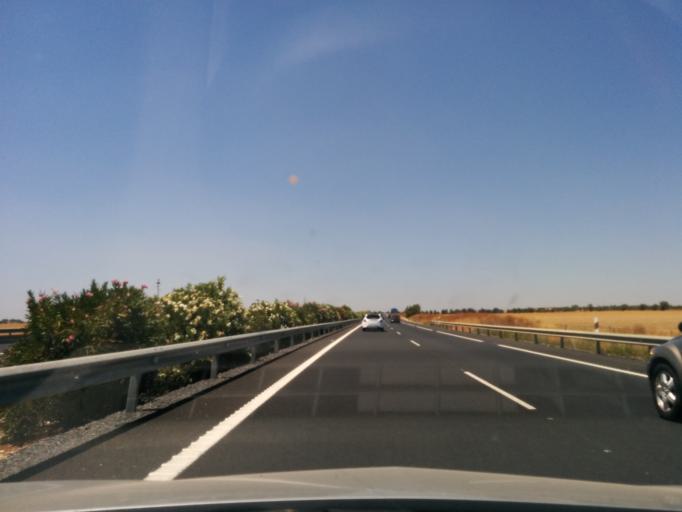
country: ES
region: Andalusia
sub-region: Provincia de Huelva
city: Lucena del Puerto
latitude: 37.3346
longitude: -6.7710
